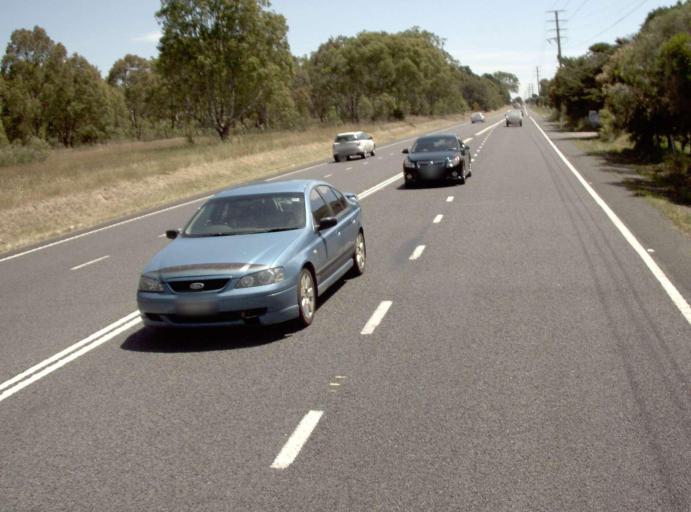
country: AU
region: Victoria
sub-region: Latrobe
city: Traralgon
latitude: -38.1785
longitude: 146.6314
